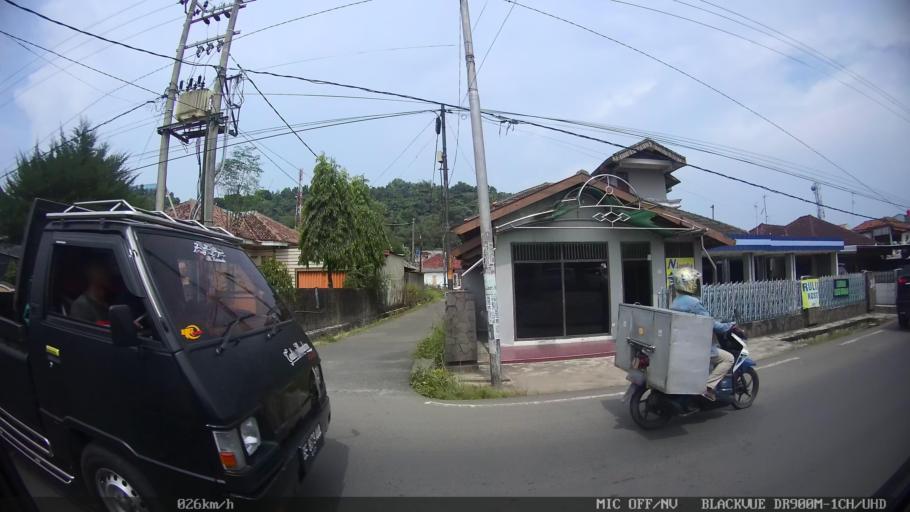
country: ID
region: Lampung
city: Bandarlampung
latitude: -5.4311
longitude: 105.2768
